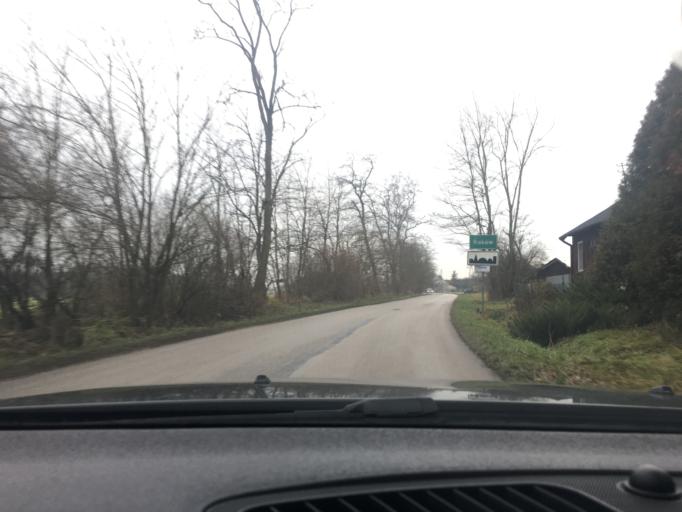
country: PL
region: Swietokrzyskie
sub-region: Powiat jedrzejowski
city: Imielno
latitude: 50.6422
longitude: 20.3954
